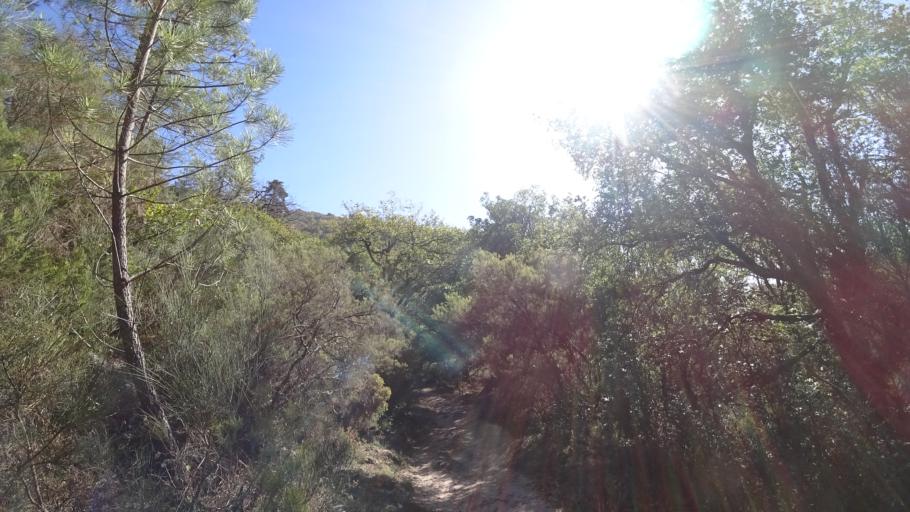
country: PT
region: Braga
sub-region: Vieira do Minho
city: Real
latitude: 41.7553
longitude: -8.1500
